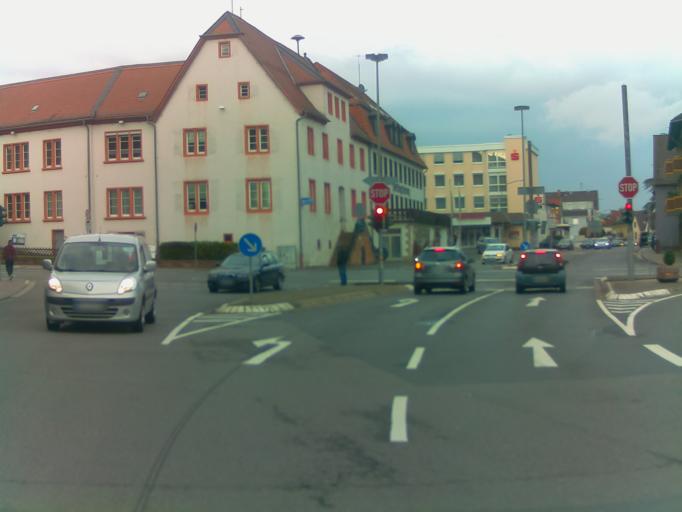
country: DE
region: Hesse
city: Hochst im Odenwald
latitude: 49.7992
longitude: 8.9937
